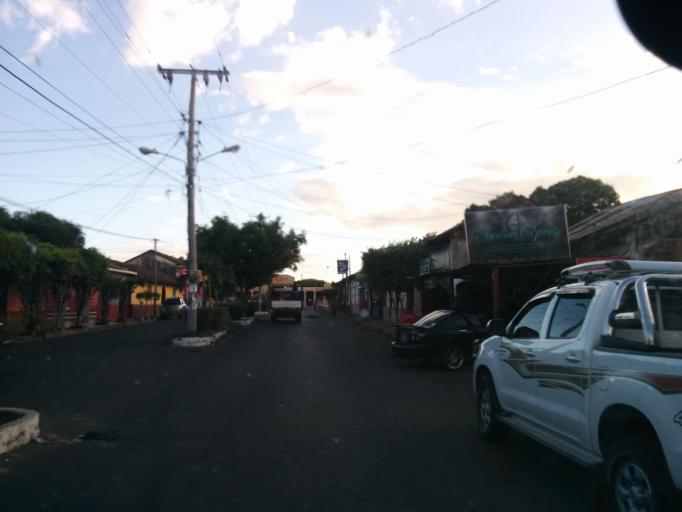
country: NI
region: Leon
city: Leon
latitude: 12.4250
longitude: -86.8778
